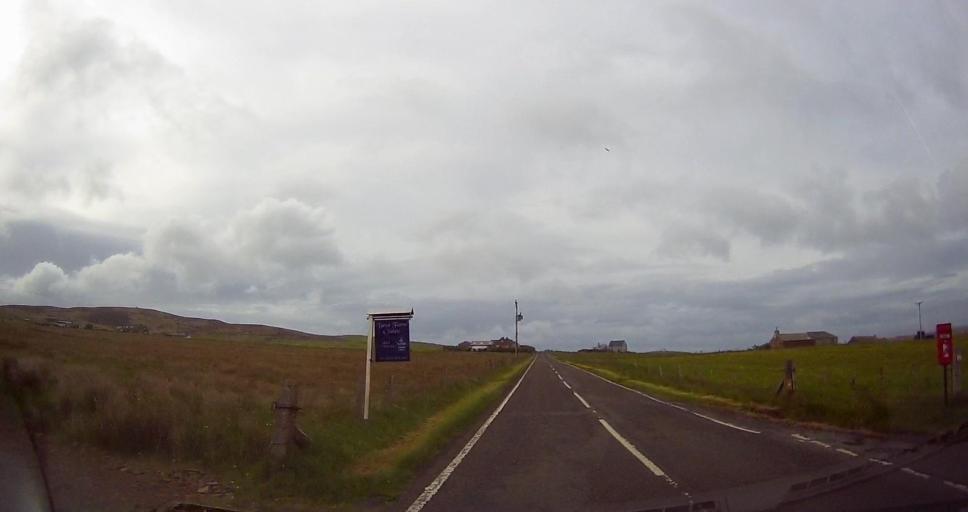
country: GB
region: Scotland
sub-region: Orkney Islands
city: Stromness
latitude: 58.9345
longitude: -3.2104
